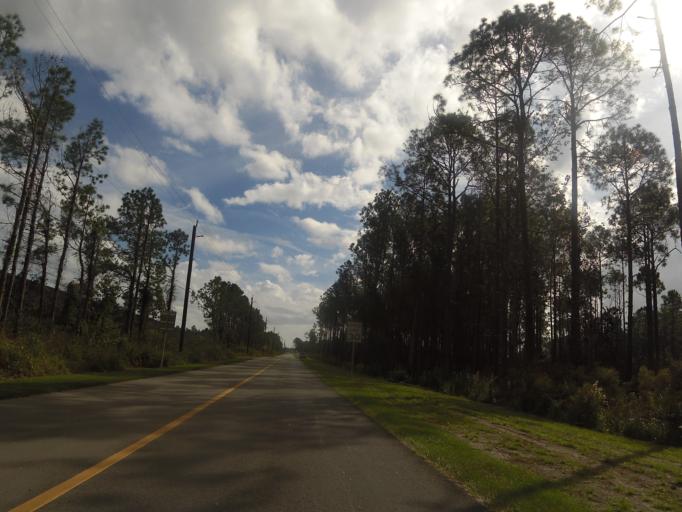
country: US
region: Florida
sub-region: Saint Johns County
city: Villano Beach
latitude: 29.9953
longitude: -81.3927
